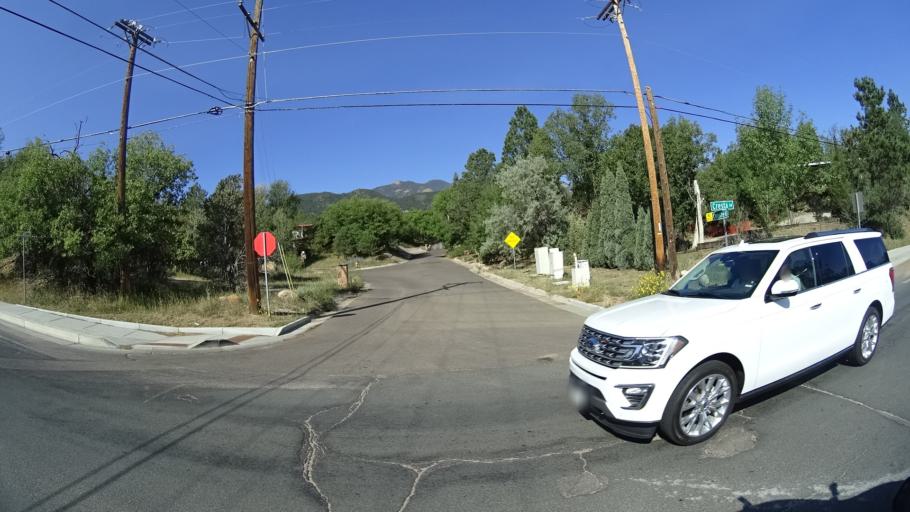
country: US
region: Colorado
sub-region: El Paso County
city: Colorado Springs
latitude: 38.8112
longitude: -104.8580
